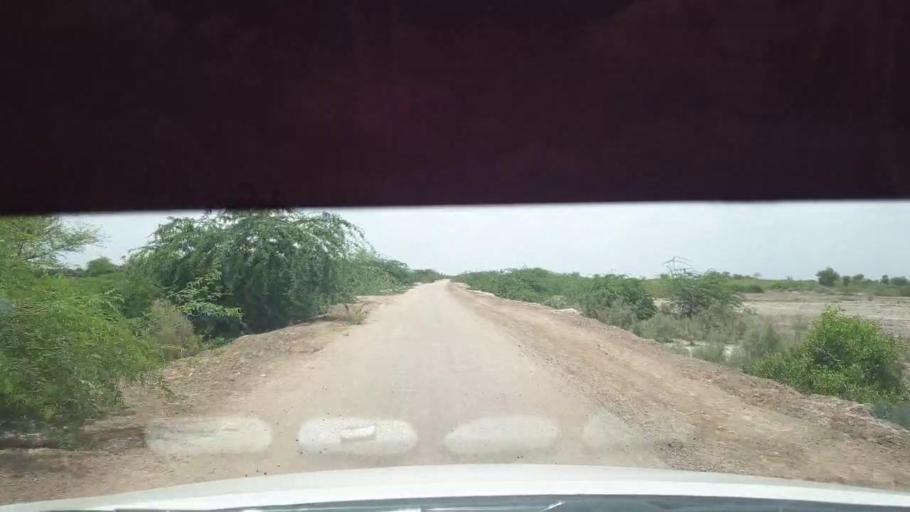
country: PK
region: Sindh
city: Kadhan
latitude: 24.5261
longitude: 69.0898
